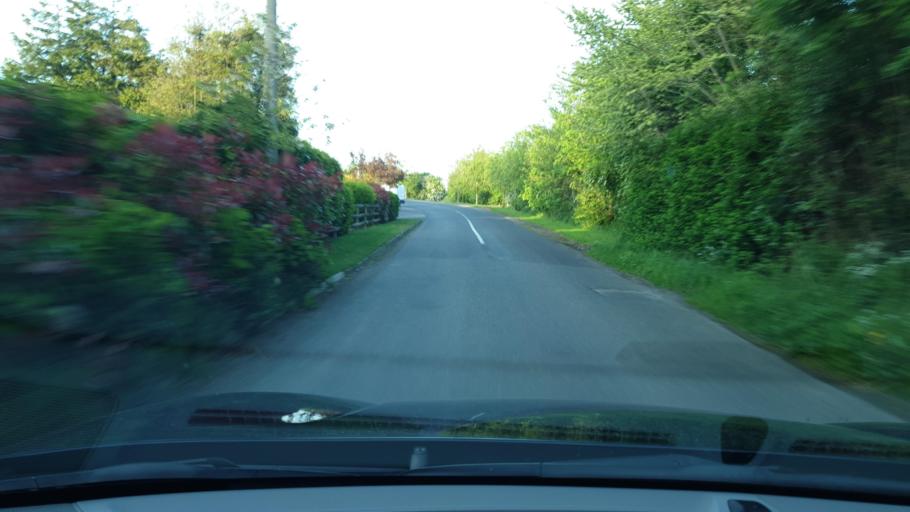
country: IE
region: Leinster
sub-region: An Mhi
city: Ashbourne
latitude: 53.4891
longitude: -6.3982
